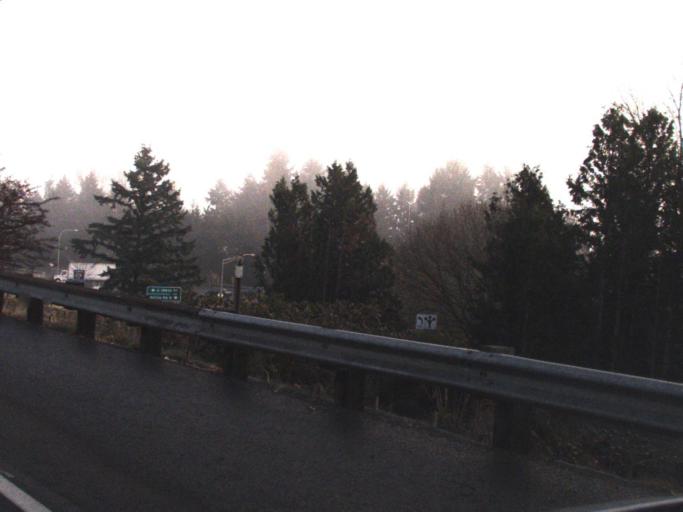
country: US
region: Washington
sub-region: King County
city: SeaTac
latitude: 47.4306
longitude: -122.2720
